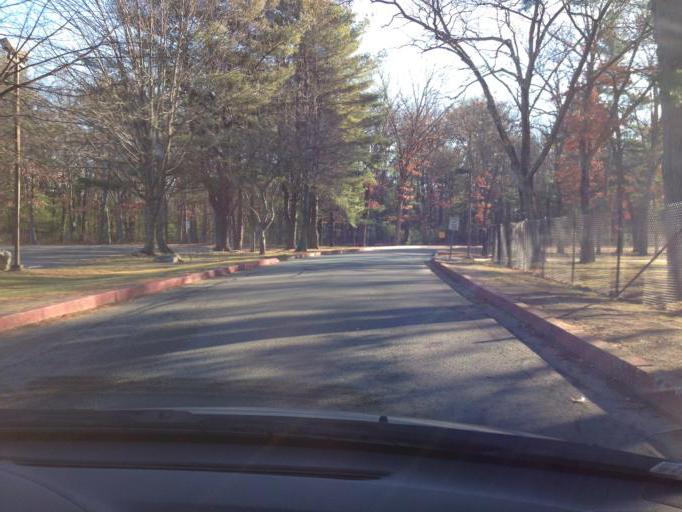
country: US
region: Massachusetts
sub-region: Middlesex County
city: Bedford
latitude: 42.5089
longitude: -71.2754
